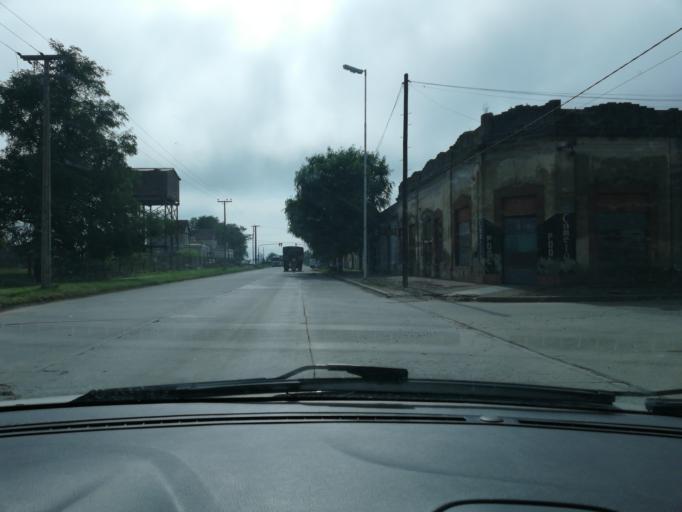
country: AR
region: Buenos Aires
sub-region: Partido de Balcarce
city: Balcarce
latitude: -37.8359
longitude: -58.2652
